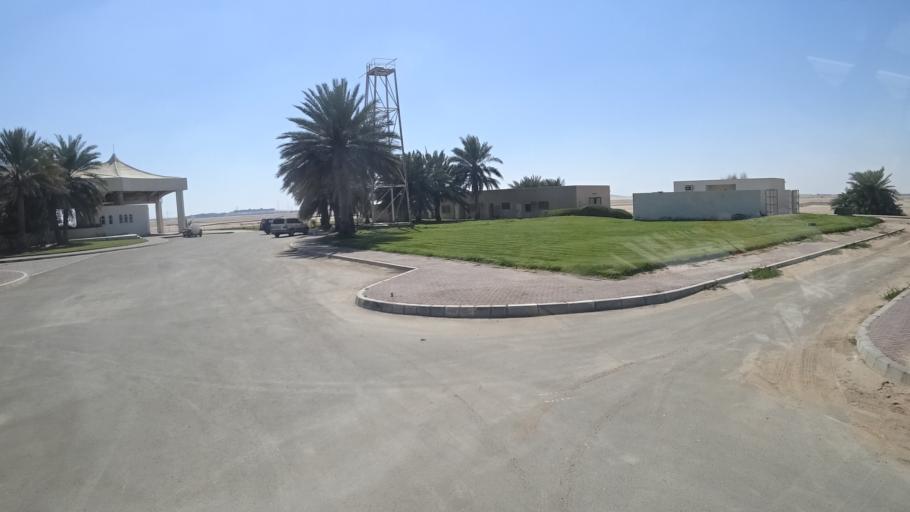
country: AE
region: Abu Dhabi
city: Abu Dhabi
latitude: 24.2171
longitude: 54.7398
